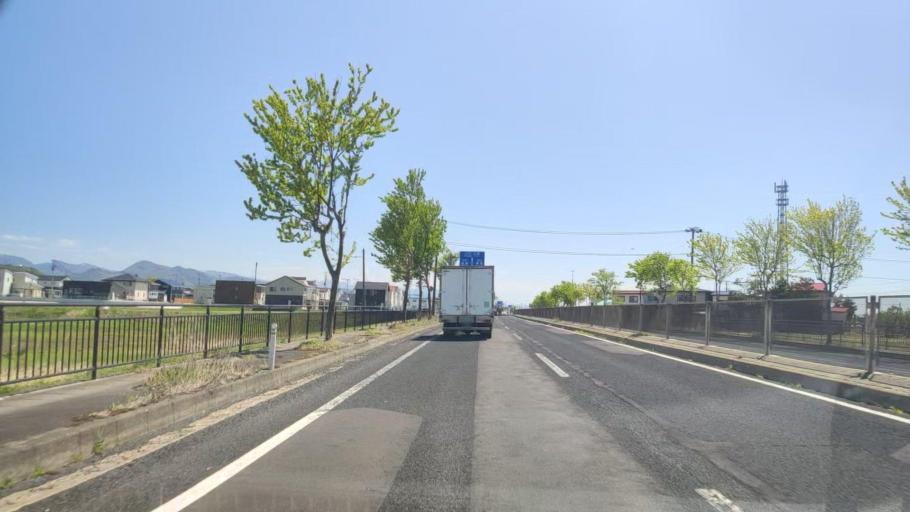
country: JP
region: Yamagata
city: Higashine
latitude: 38.4535
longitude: 140.3824
